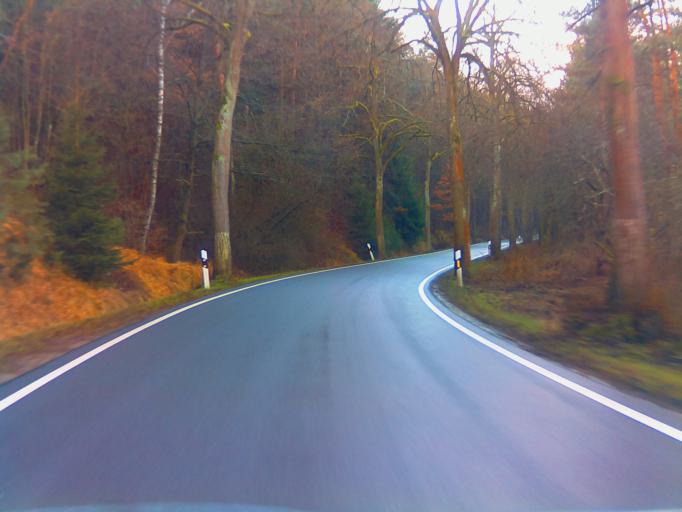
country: DE
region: Thuringia
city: Gossel
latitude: 50.8143
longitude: 10.8611
